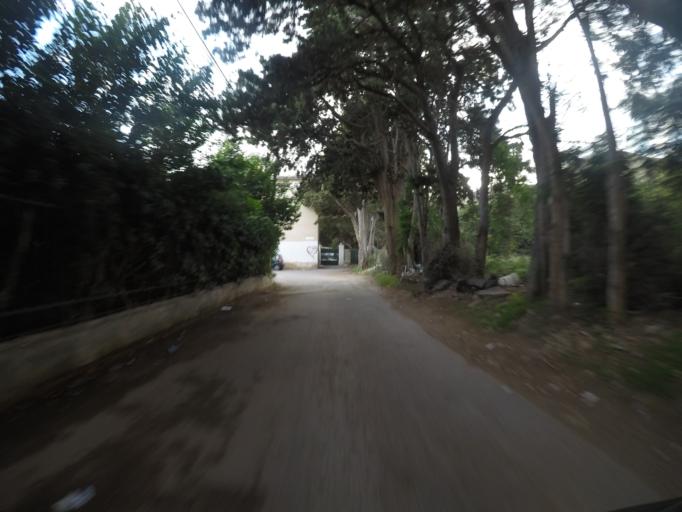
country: IT
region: Sicily
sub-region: Palermo
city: Isola delle Femmine
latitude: 38.1999
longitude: 13.3095
